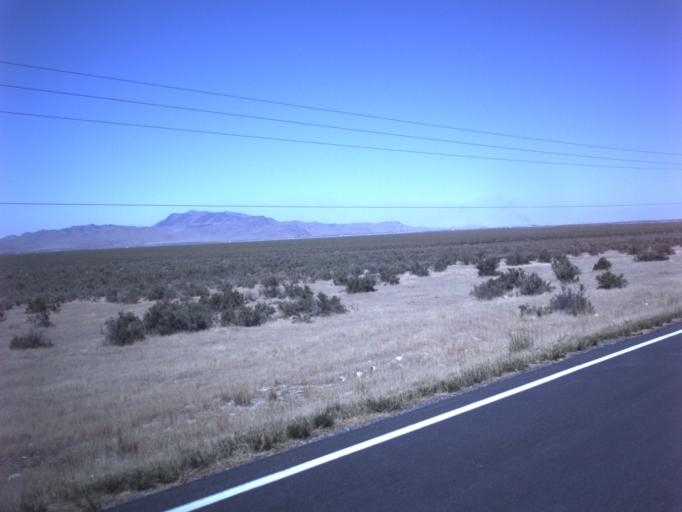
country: US
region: Utah
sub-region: Tooele County
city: Grantsville
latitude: 40.6996
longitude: -112.6660
